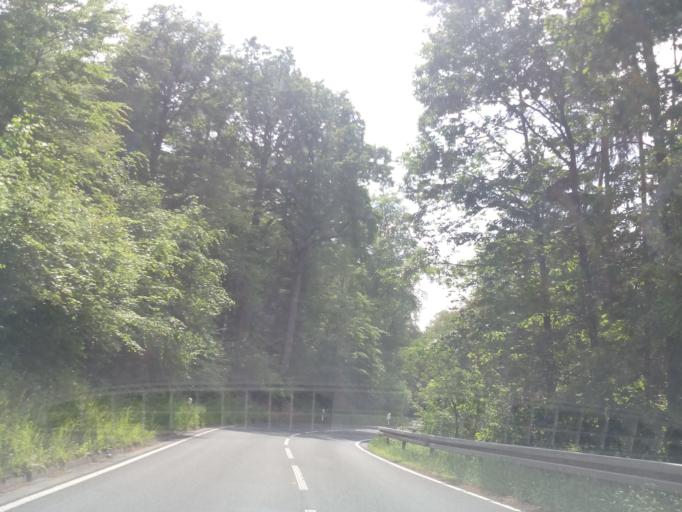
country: DE
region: Thuringia
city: Hellingen
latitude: 50.2754
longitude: 10.7510
